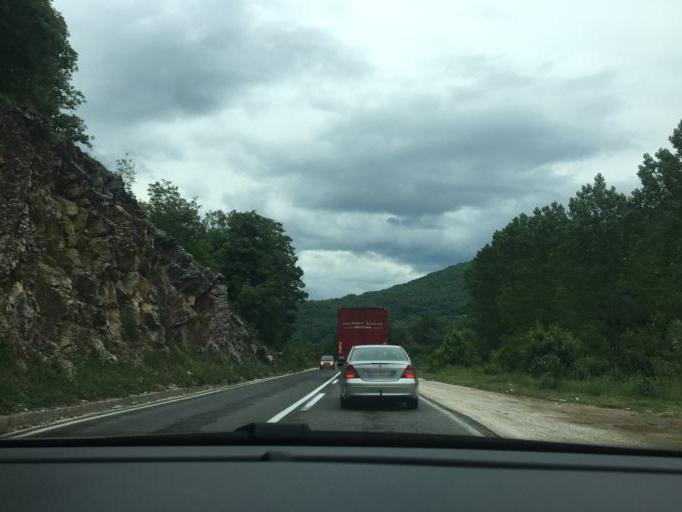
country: MK
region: Drugovo
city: Drugovo
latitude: 41.4779
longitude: 20.8762
